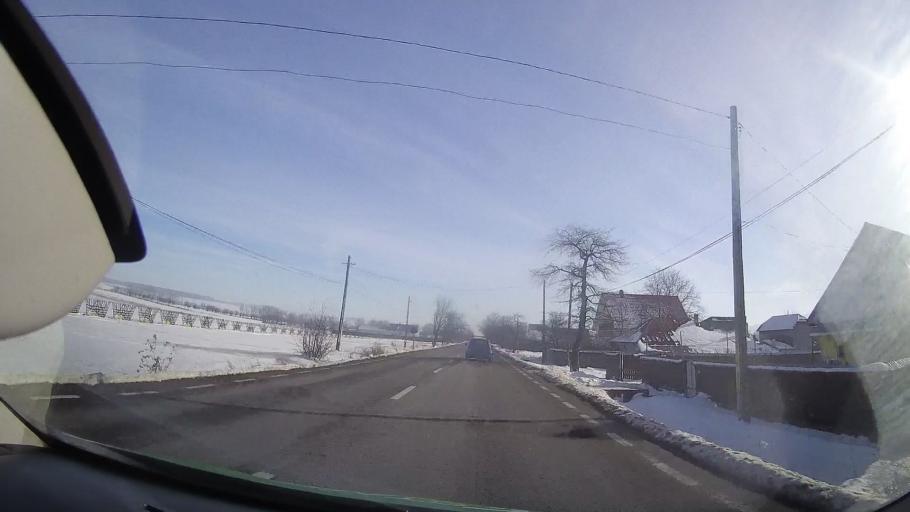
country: RO
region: Neamt
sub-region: Comuna Negresti
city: Negresti
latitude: 47.0598
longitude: 26.3862
